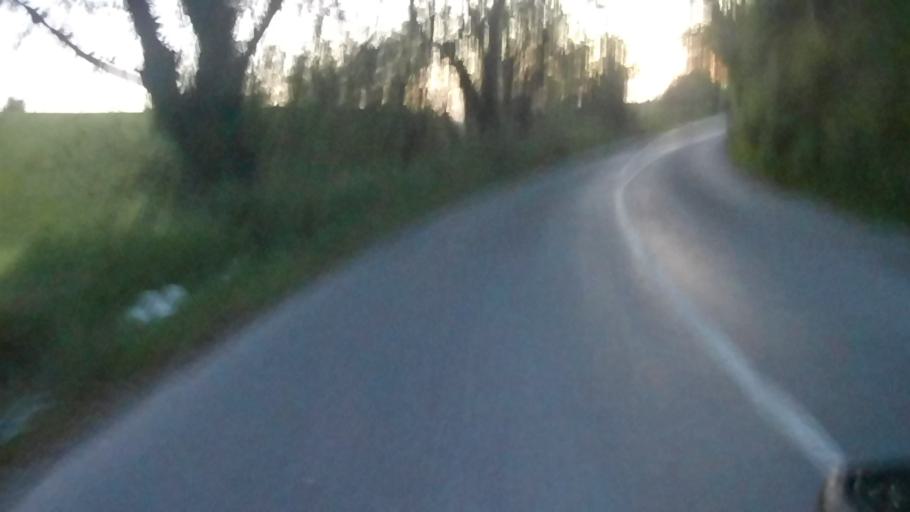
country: IE
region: Munster
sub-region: County Cork
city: Carrigtwohill
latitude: 51.9377
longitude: -8.3217
